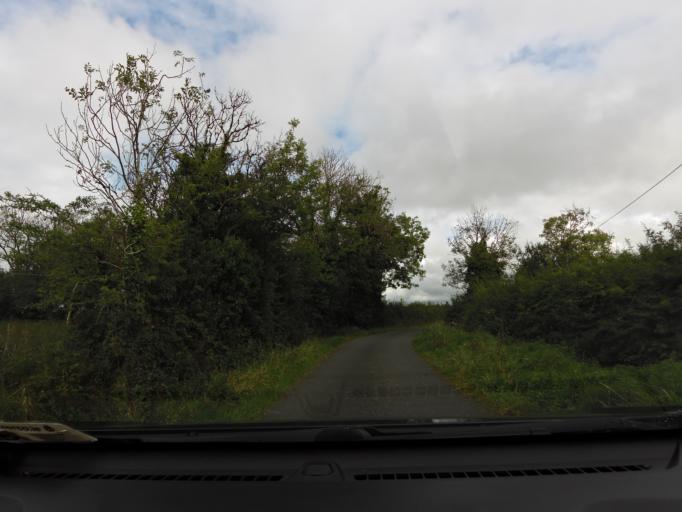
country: IE
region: Connaught
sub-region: County Galway
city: Loughrea
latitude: 53.2976
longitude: -8.6008
